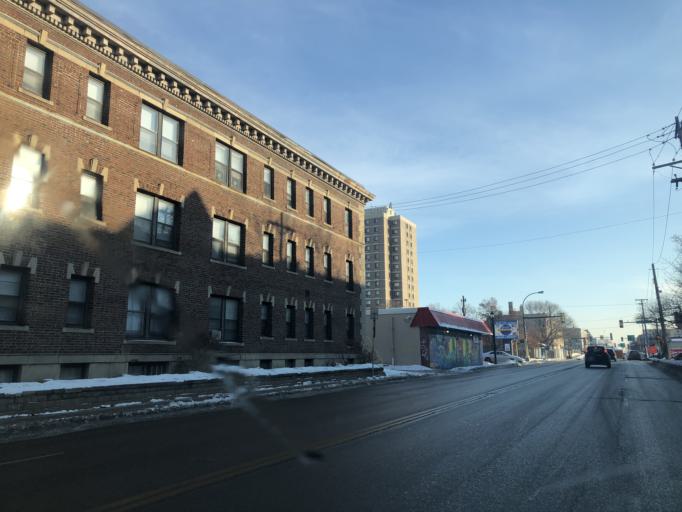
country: US
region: Minnesota
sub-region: Hennepin County
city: Minneapolis
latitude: 44.9627
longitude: -93.2726
